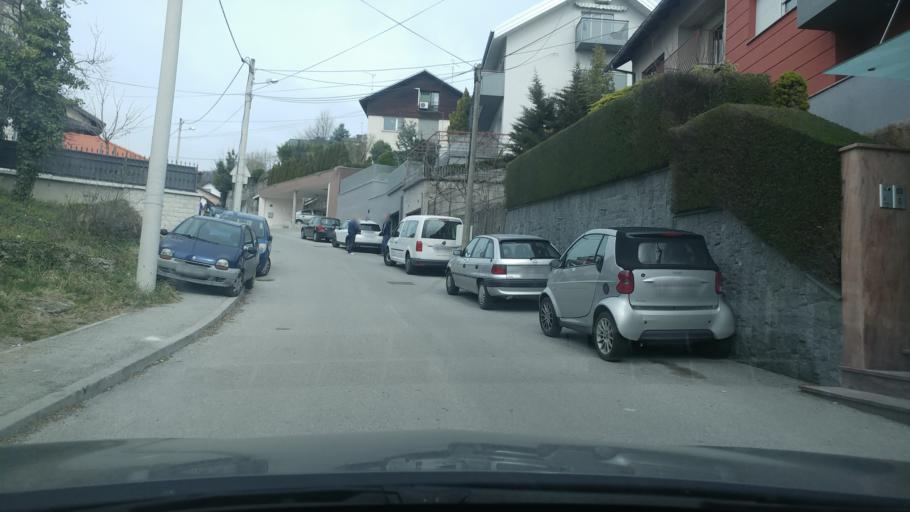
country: HR
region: Grad Zagreb
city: Zagreb
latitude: 45.8483
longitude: 15.9285
